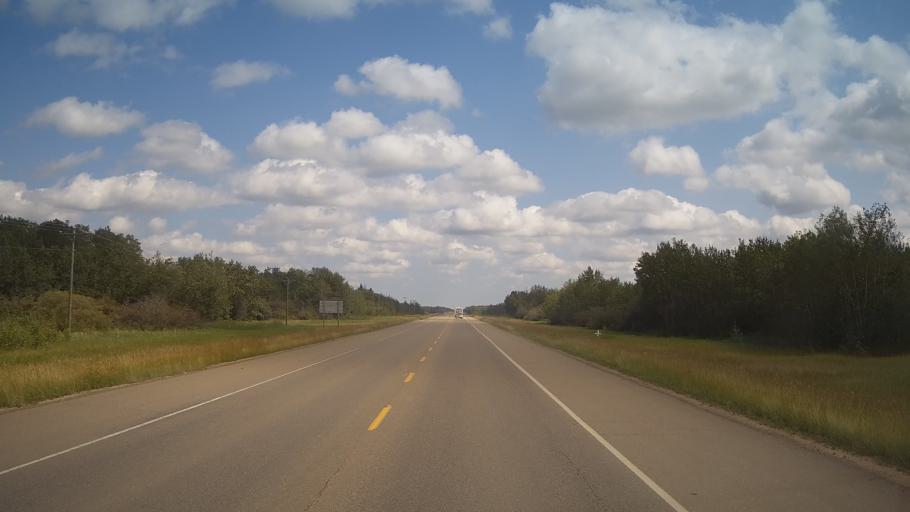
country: CA
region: Alberta
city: Sherwood Park
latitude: 53.3957
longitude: -113.0915
